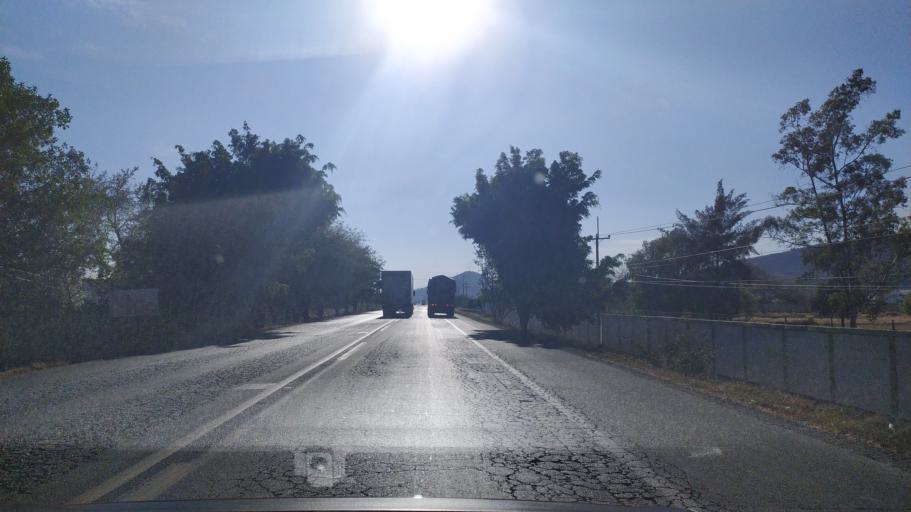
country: MX
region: Jalisco
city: Jamay
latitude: 20.2942
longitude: -102.6773
